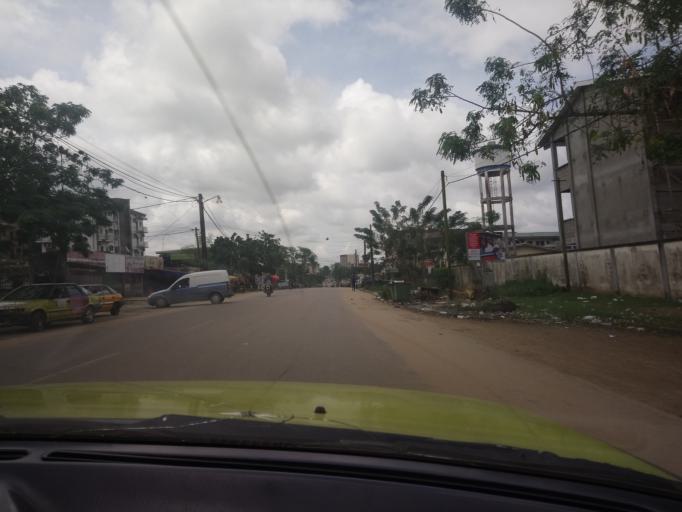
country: CM
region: Littoral
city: Douala
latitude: 4.0946
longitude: 9.7410
